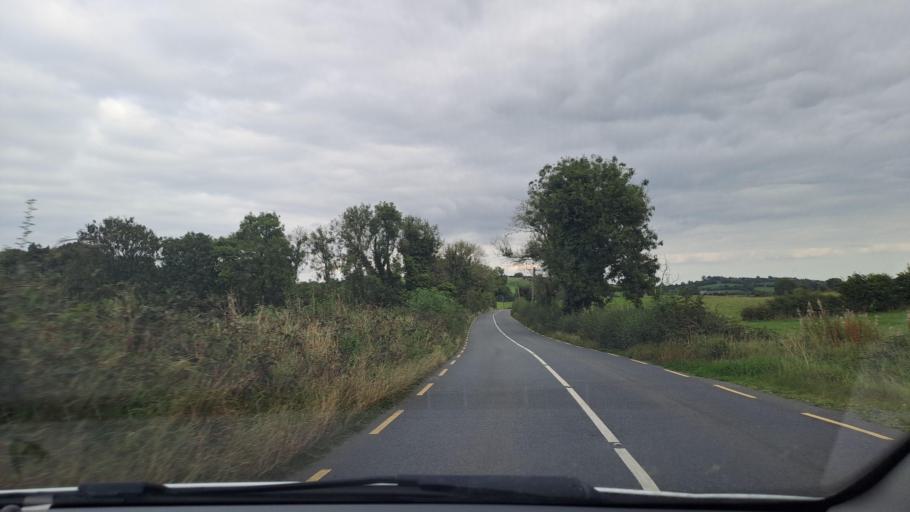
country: IE
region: Ulster
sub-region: County Monaghan
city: Carrickmacross
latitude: 53.9976
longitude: -6.8030
